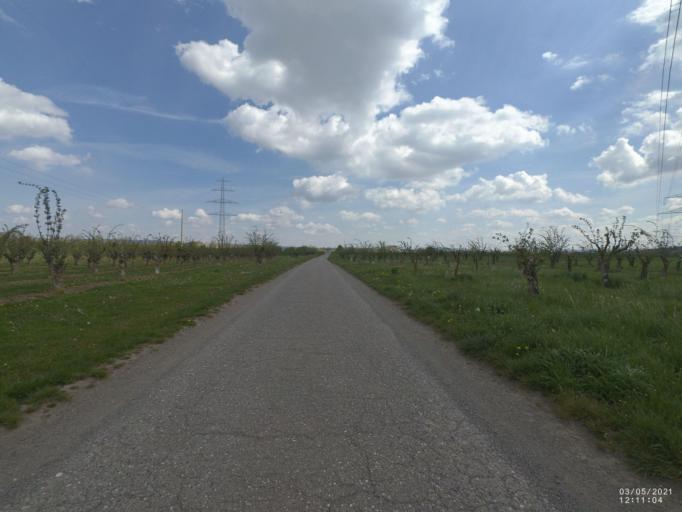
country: DE
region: Rheinland-Pfalz
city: Kettig
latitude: 50.3999
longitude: 7.4754
